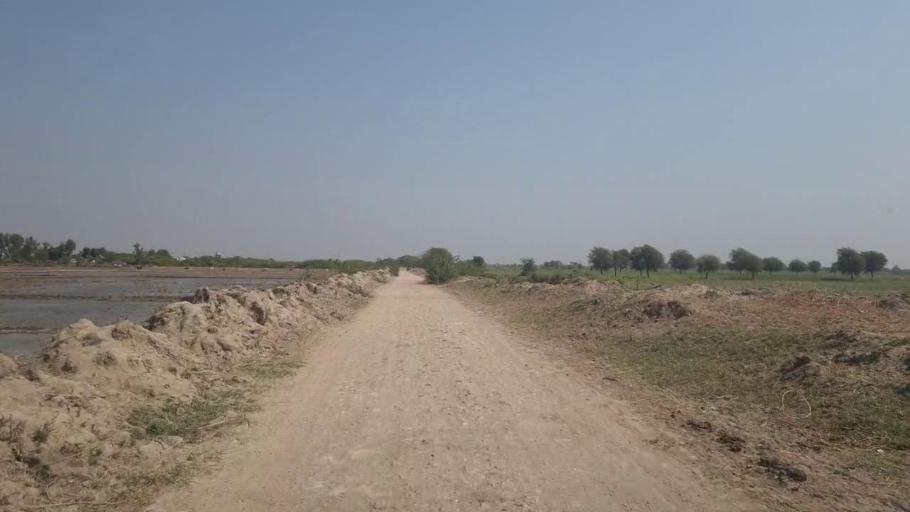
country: PK
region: Sindh
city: Dhoro Naro
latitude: 25.4850
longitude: 69.5484
